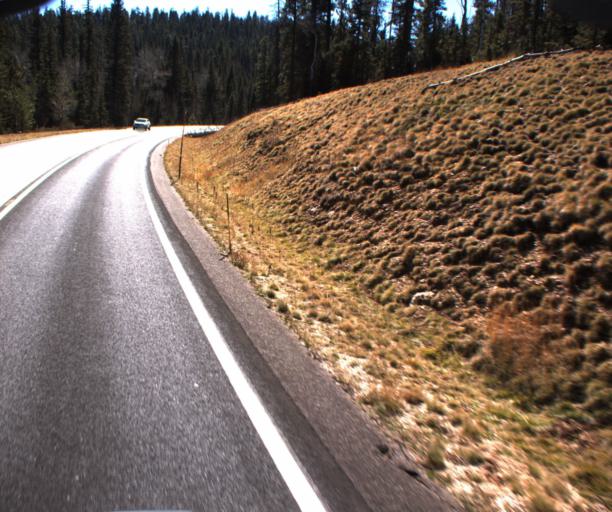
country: US
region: Arizona
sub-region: Coconino County
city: Grand Canyon
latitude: 36.5220
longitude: -112.1398
